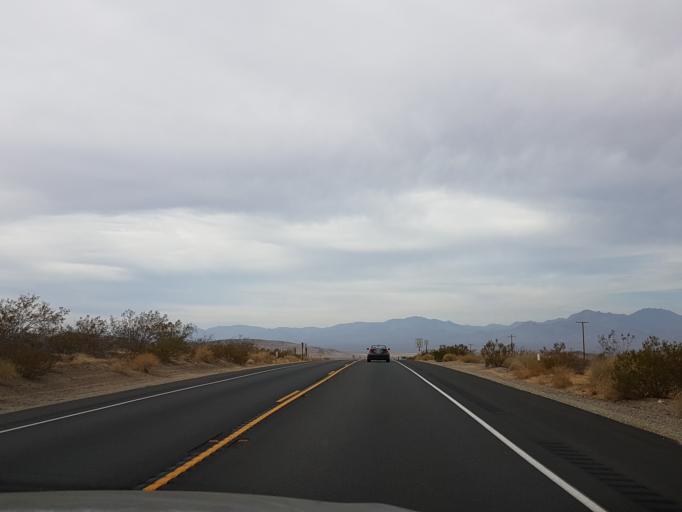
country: US
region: California
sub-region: Kern County
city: Ridgecrest
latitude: 35.5477
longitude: -117.7053
